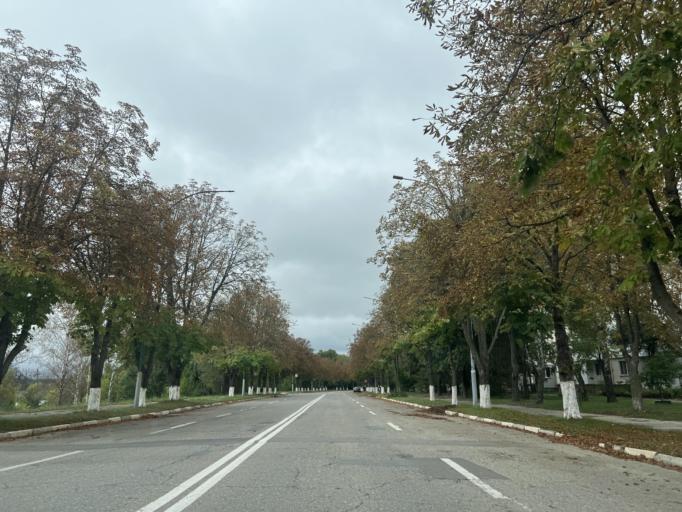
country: MD
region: Ungheni
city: Ungheni
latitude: 47.2158
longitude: 27.8084
